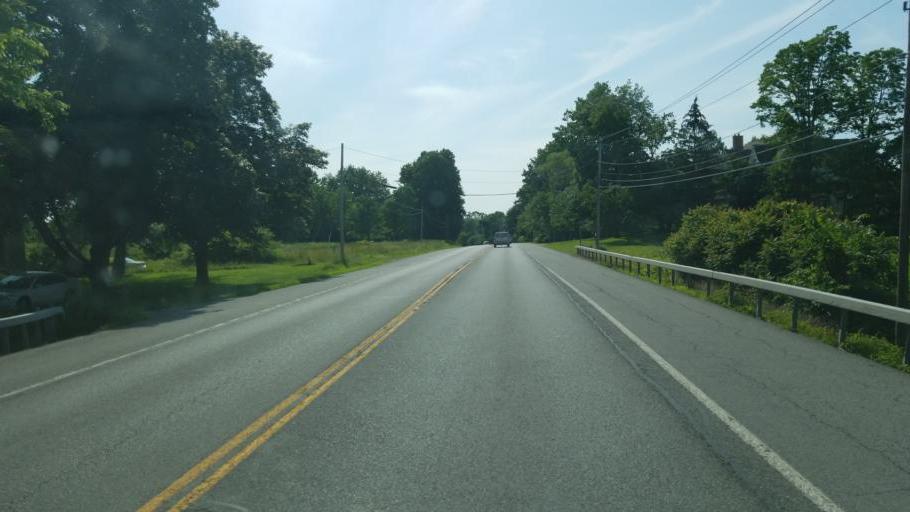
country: US
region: New York
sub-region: Monroe County
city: Honeoye Falls
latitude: 42.9056
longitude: -77.5306
